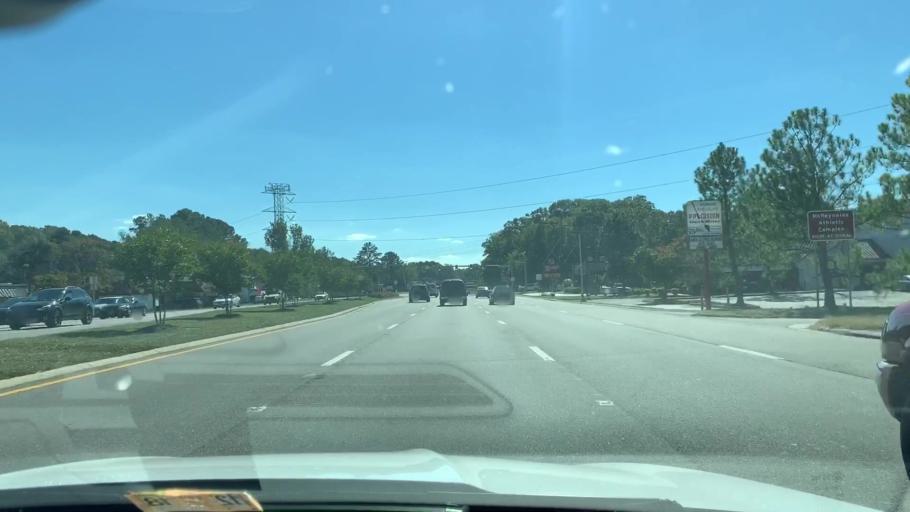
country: US
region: Virginia
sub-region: York County
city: Yorktown
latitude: 37.1467
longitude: -76.4588
